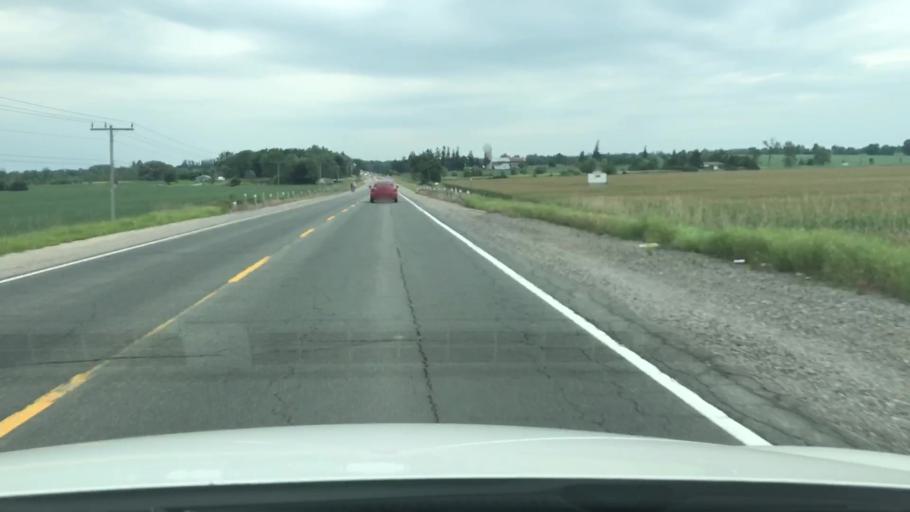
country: CA
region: Ontario
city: Innisfil
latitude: 44.3080
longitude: -79.6152
